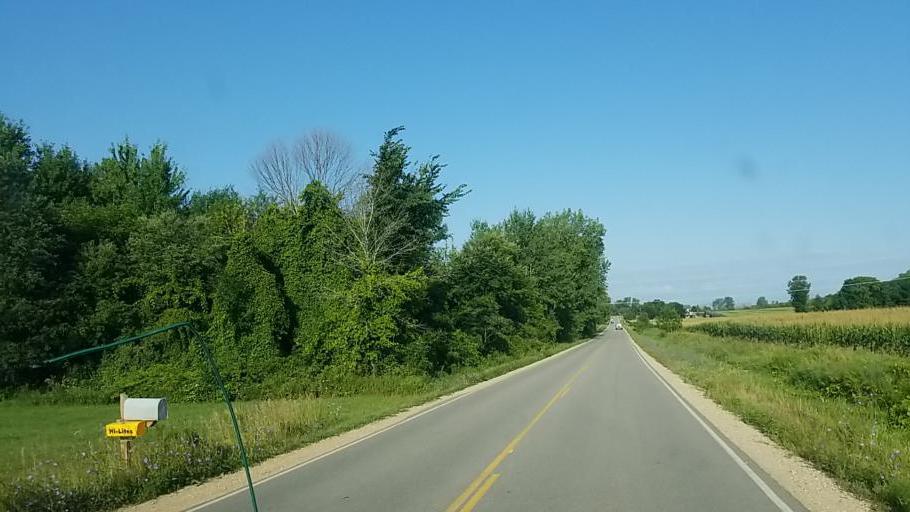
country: US
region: Michigan
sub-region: Newaygo County
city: Newaygo
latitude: 43.3511
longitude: -85.8253
